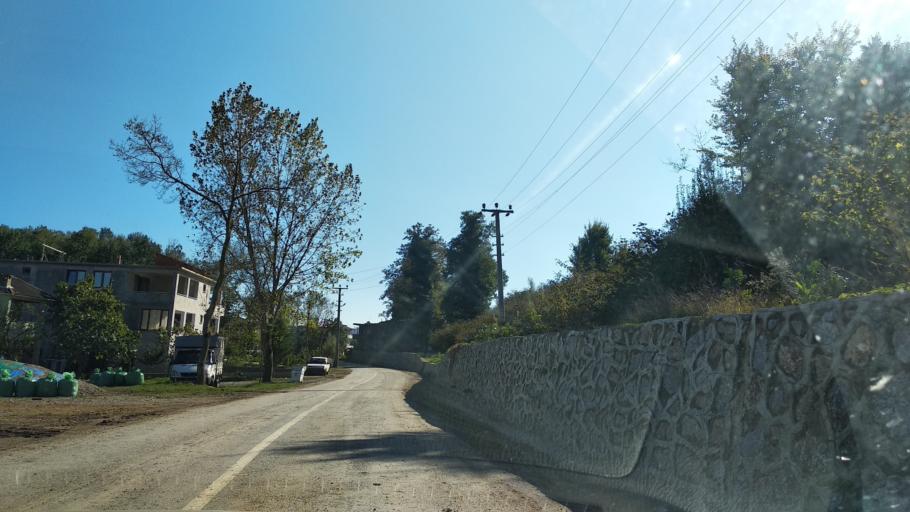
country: TR
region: Sakarya
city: Ortakoy
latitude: 41.0323
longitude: 30.5954
